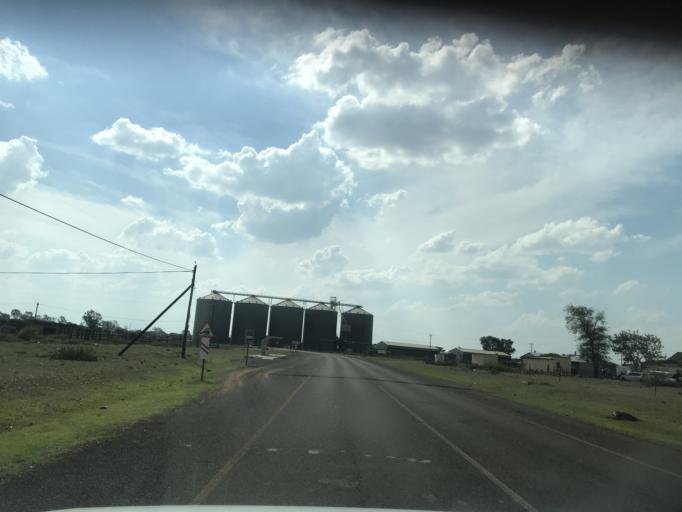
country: BW
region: South East
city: Janeng
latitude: -25.4745
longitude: 25.6035
